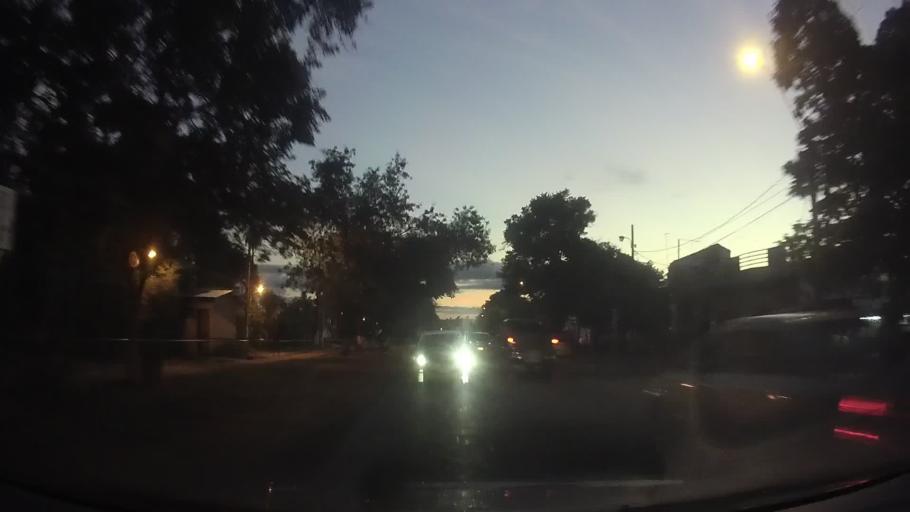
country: PY
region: Central
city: Itaugua
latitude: -25.3953
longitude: -57.3565
